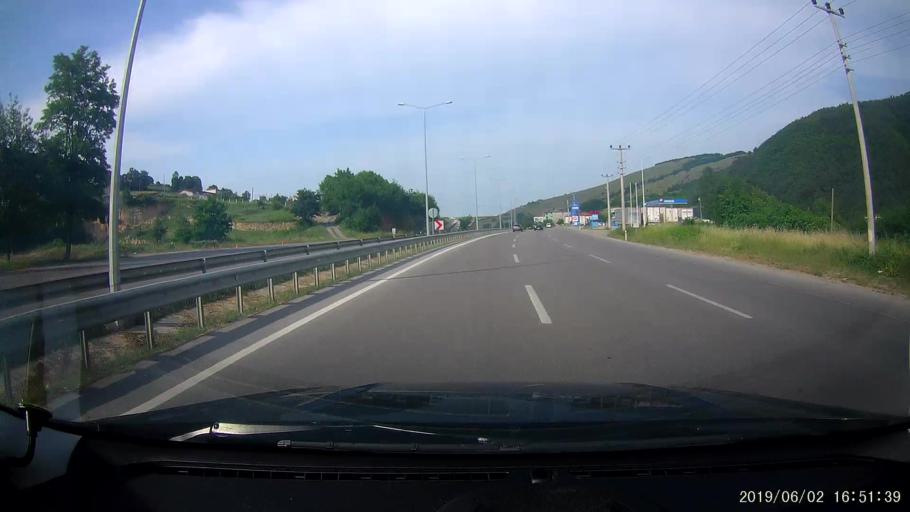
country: TR
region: Samsun
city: Taflan
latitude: 41.2766
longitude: 36.1856
